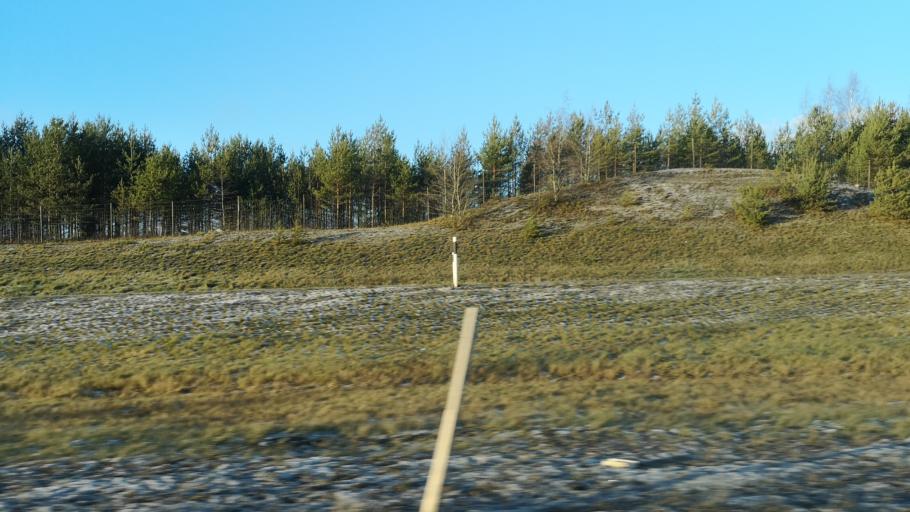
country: FI
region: Paijanne Tavastia
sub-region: Lahti
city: Heinola
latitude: 61.1613
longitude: 25.9943
